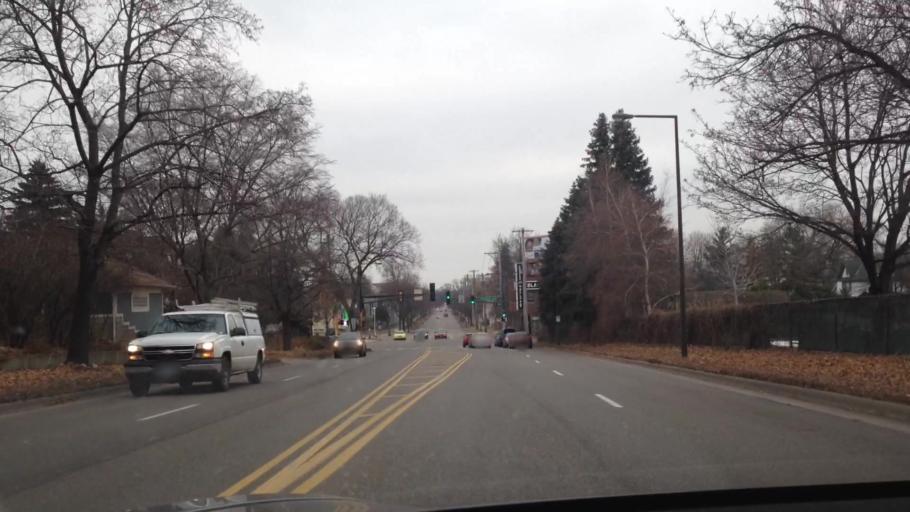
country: US
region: Minnesota
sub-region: Ramsey County
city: Falcon Heights
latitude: 44.9496
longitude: -93.1925
